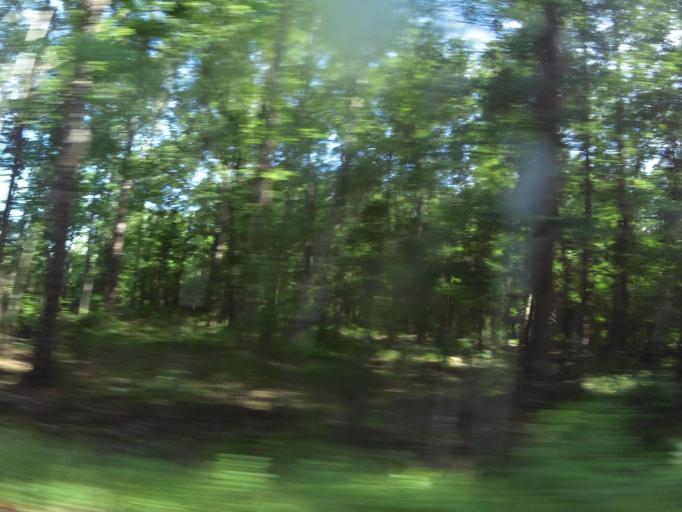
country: US
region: Florida
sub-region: Nassau County
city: Callahan
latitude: 30.5614
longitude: -81.8427
